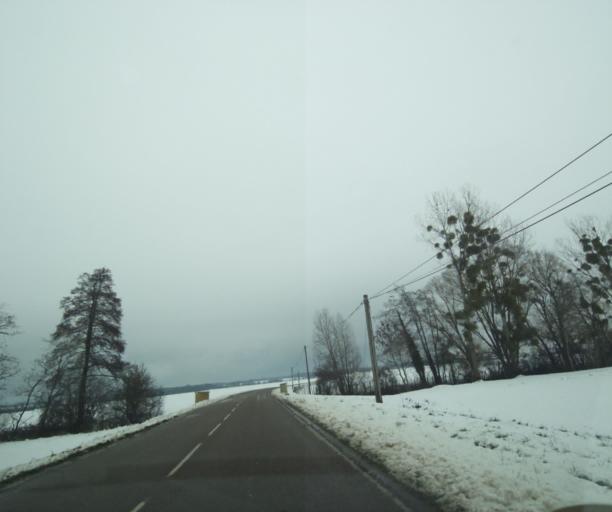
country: FR
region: Champagne-Ardenne
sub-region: Departement de la Haute-Marne
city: Montier-en-Der
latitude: 48.4477
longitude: 4.7906
